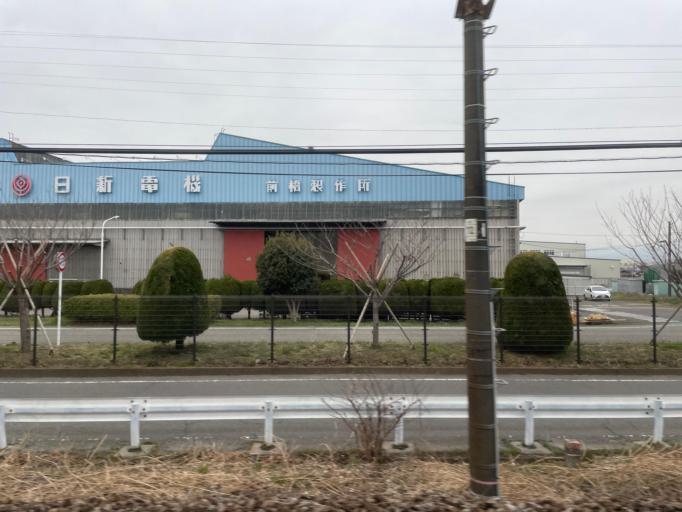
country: JP
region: Gunma
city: Maebashi-shi
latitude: 36.4108
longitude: 139.0334
